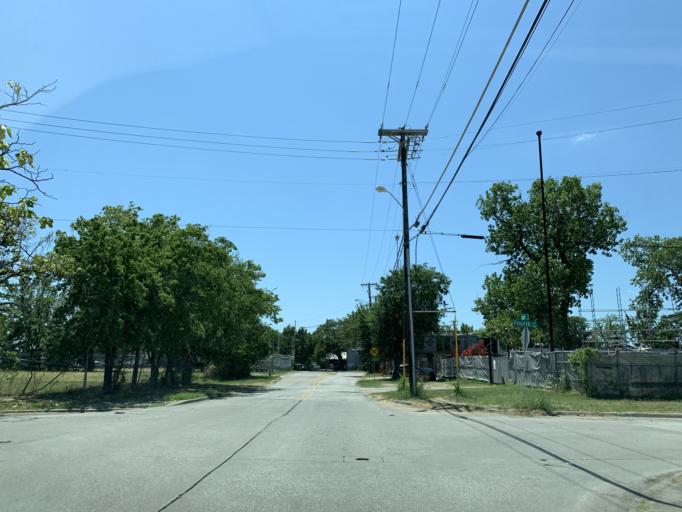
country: US
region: Texas
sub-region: Dallas County
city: Dallas
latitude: 32.7793
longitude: -96.7694
